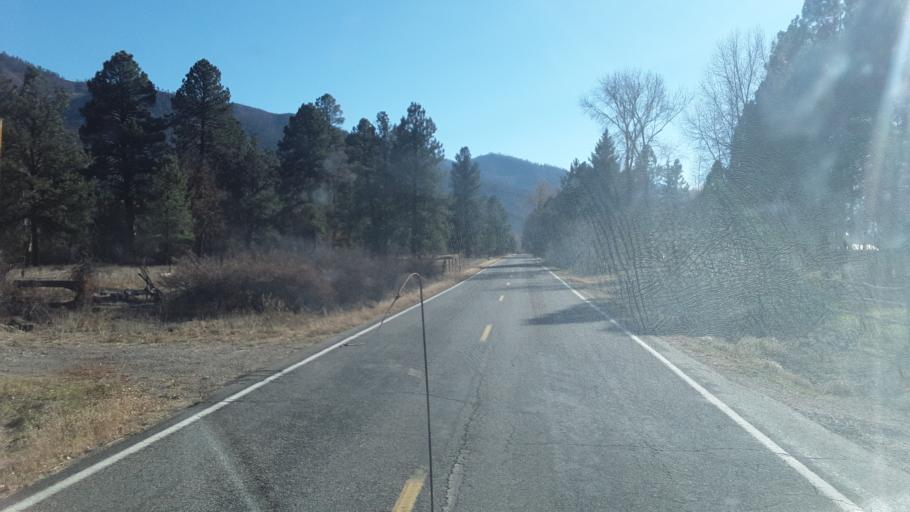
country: US
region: Colorado
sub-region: La Plata County
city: Durango
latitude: 37.4422
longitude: -107.7994
